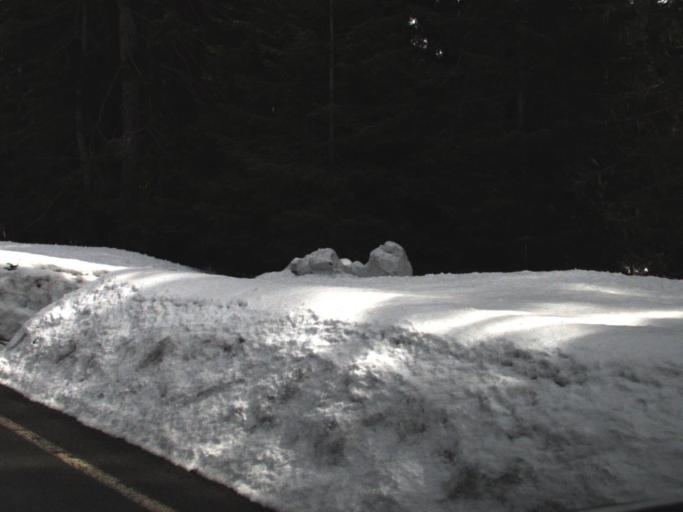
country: US
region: Washington
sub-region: Kittitas County
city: Cle Elum
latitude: 46.9394
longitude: -121.3422
